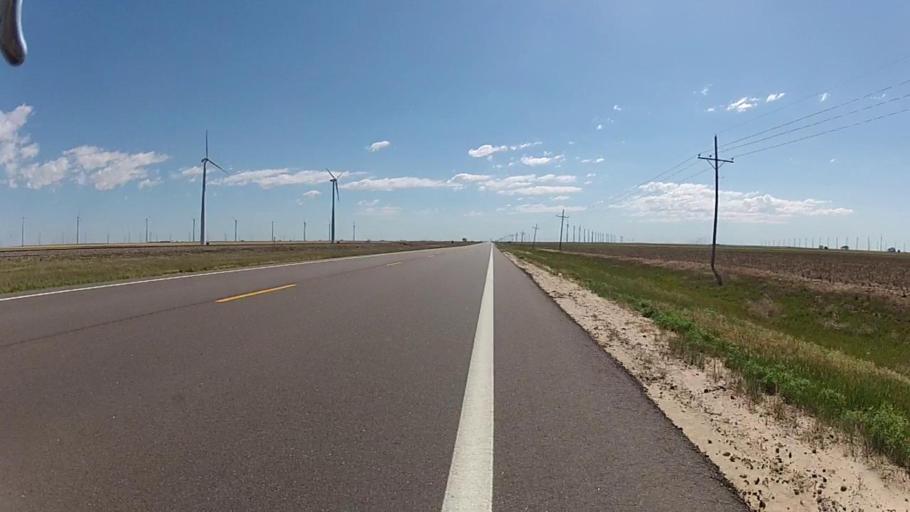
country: US
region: Kansas
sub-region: Gray County
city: Cimarron
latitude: 37.6106
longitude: -100.4025
